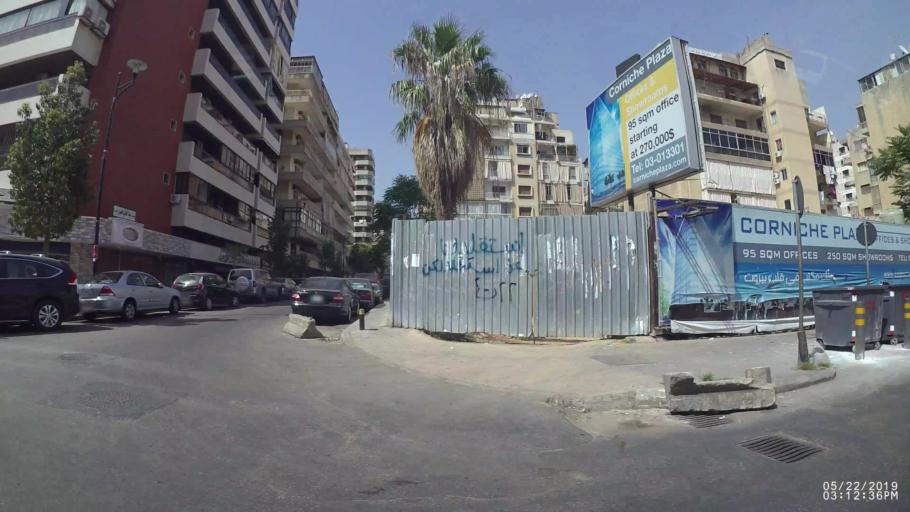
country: LB
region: Beyrouth
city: Beirut
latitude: 33.8801
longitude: 35.4937
